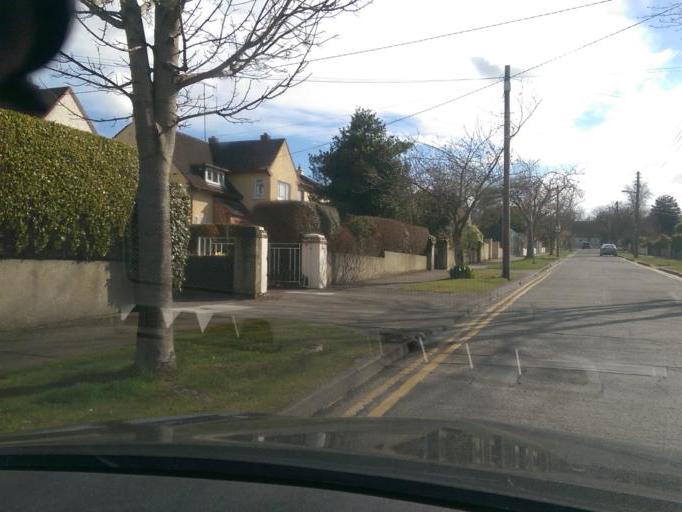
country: IE
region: Leinster
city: Malahide
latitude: 53.4490
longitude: -6.1507
